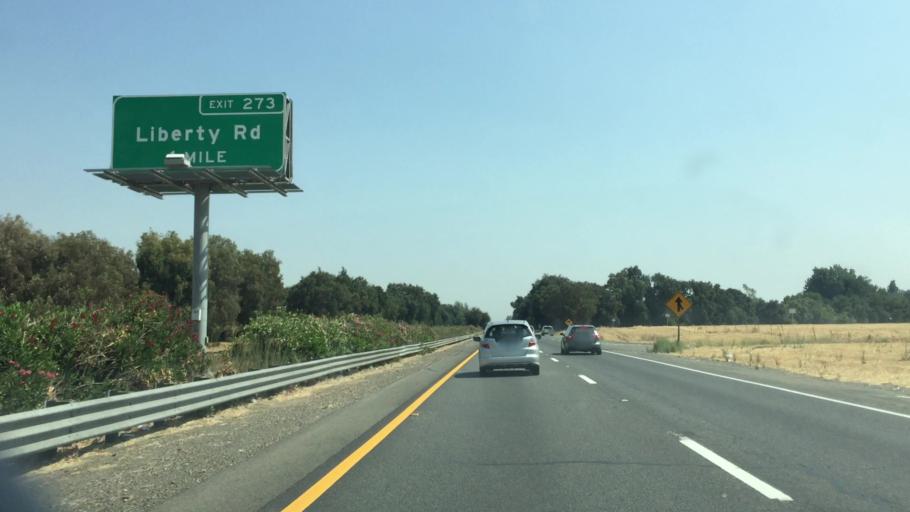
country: US
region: California
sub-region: Sacramento County
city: Galt
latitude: 38.2481
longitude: -121.2897
